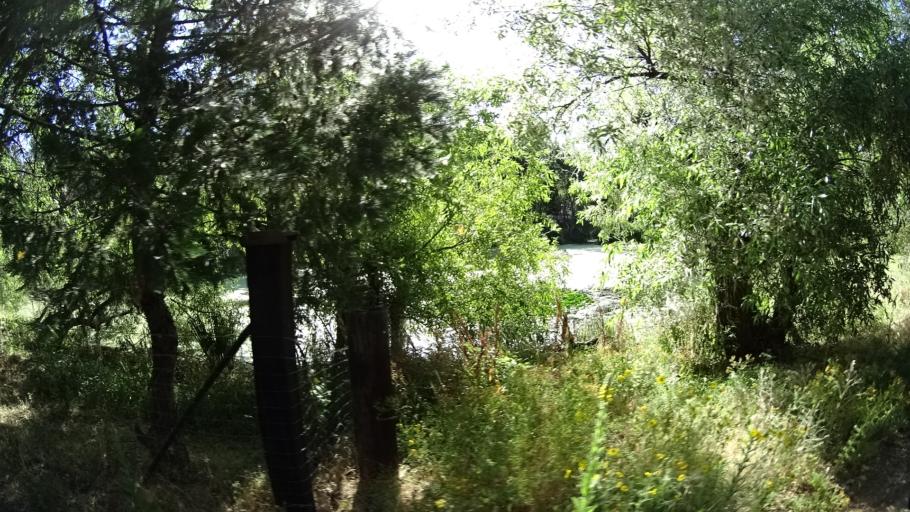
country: US
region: California
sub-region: Amador County
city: Pioneer
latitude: 38.4076
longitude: -120.5483
